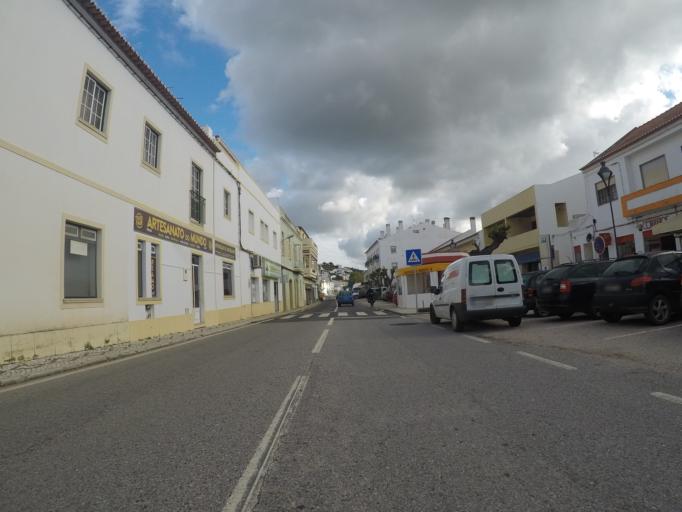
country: PT
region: Faro
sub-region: Aljezur
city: Aljezur
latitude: 37.3141
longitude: -8.8038
